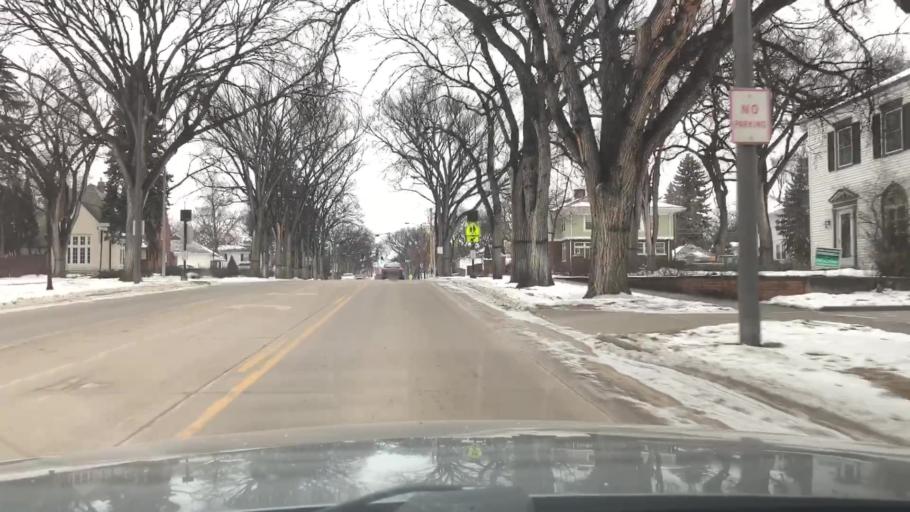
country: US
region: North Dakota
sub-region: Burleigh County
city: Bismarck
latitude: 46.8103
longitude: -100.7943
